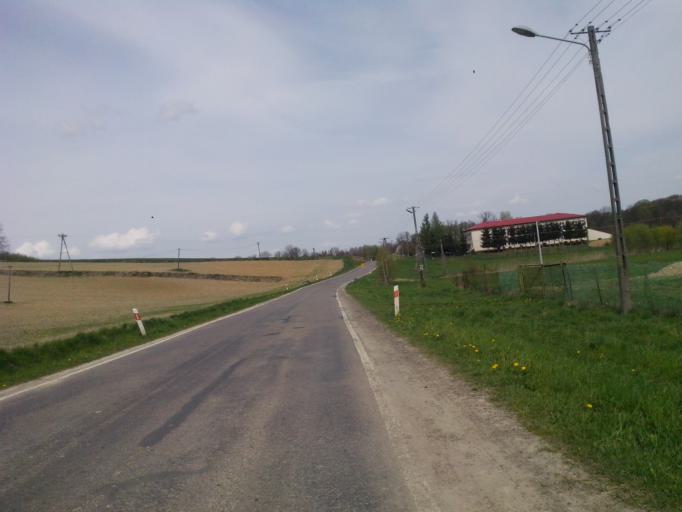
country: PL
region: Subcarpathian Voivodeship
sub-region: Powiat strzyzowski
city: Jawornik
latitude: 49.8127
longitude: 21.8441
